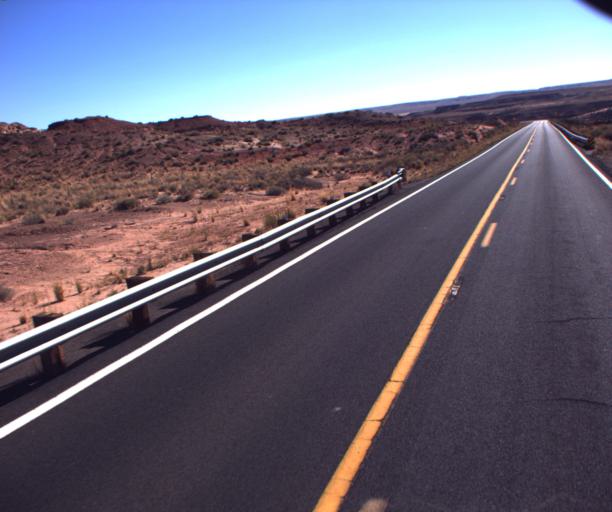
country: US
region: Arizona
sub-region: Coconino County
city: Tuba City
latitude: 36.1078
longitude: -111.2128
